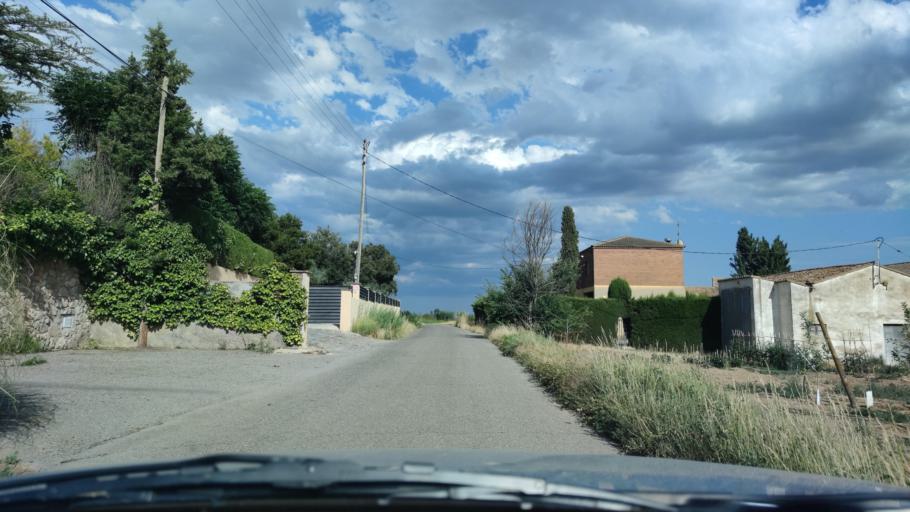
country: ES
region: Catalonia
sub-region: Provincia de Lleida
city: Lleida
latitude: 41.6293
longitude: 0.5831
